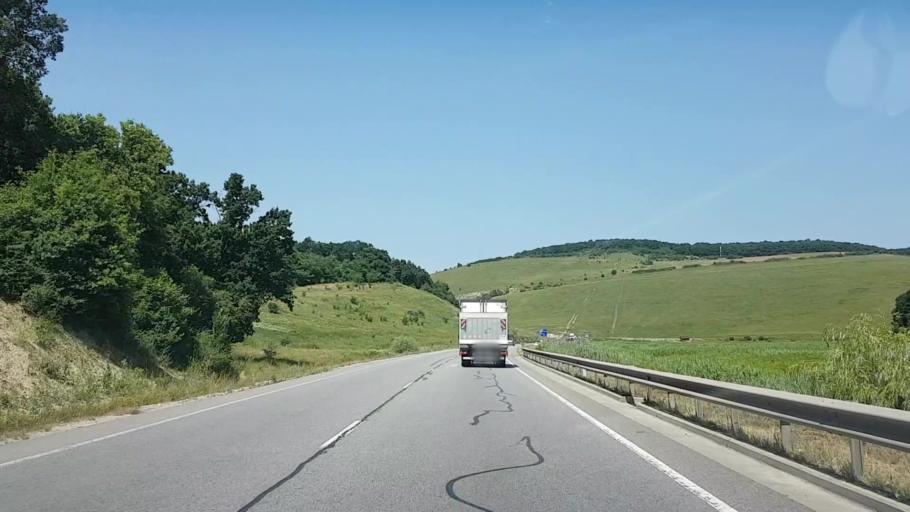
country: RO
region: Cluj
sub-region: Comuna Apahida
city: Dezmir
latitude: 46.7394
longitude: 23.7086
